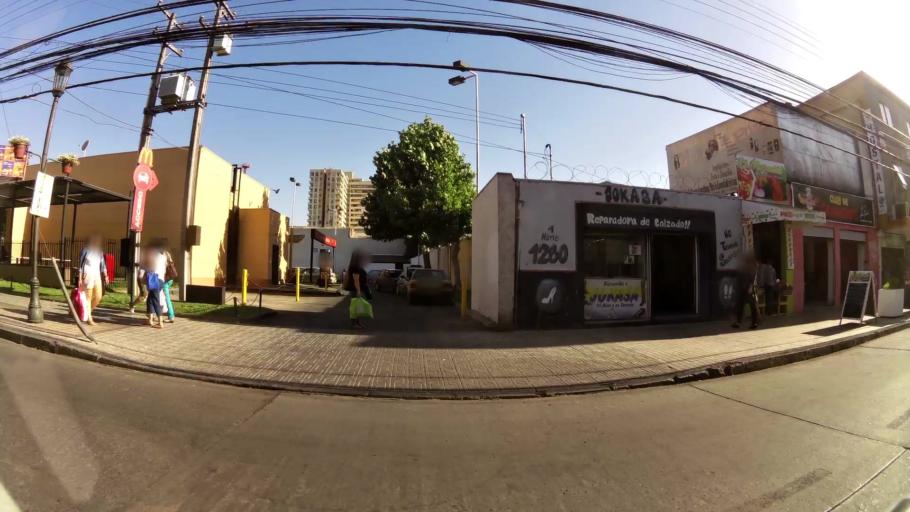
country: CL
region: Maule
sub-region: Provincia de Talca
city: Talca
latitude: -35.4266
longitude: -71.6589
